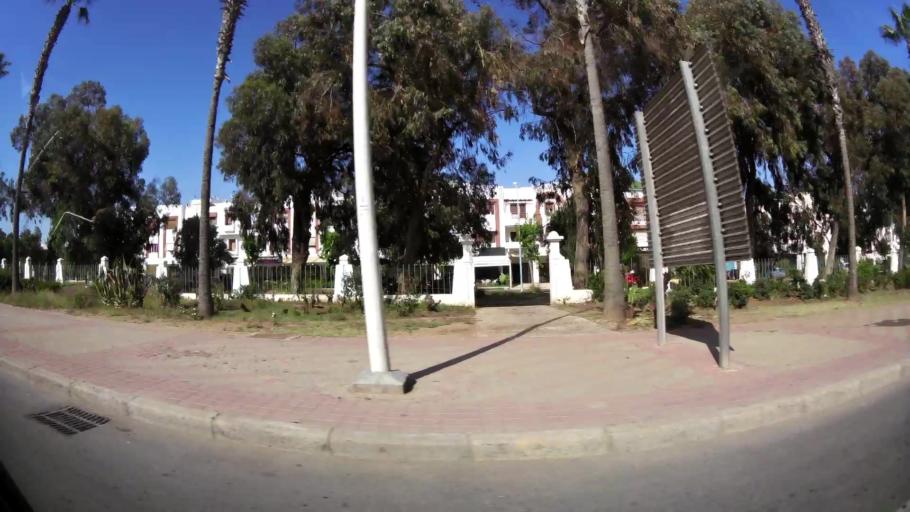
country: MA
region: Oued ed Dahab-Lagouira
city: Dakhla
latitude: 30.3886
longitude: -9.5747
